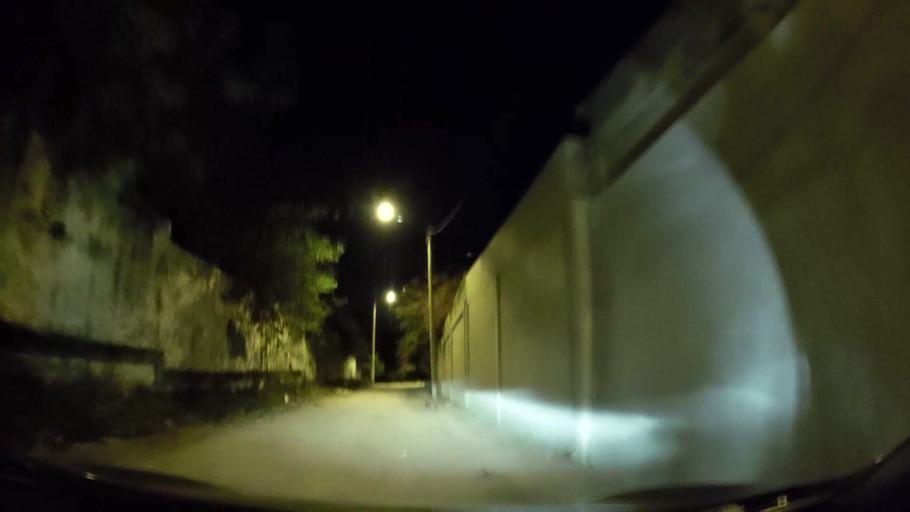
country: CO
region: Bolivar
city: Cartagena
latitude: 10.3864
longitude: -75.4970
